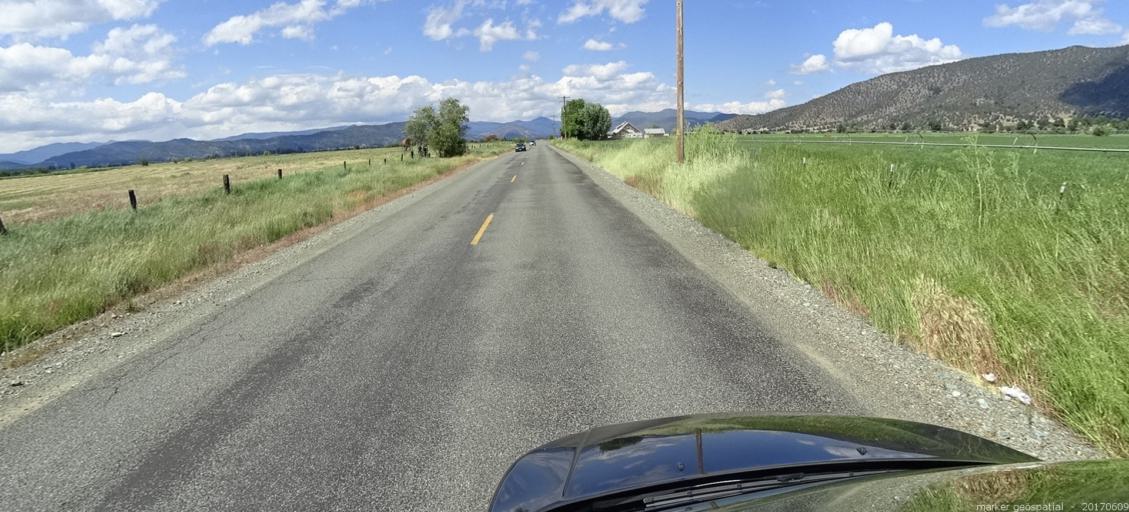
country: US
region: California
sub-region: Siskiyou County
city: Yreka
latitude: 41.4954
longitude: -122.8593
